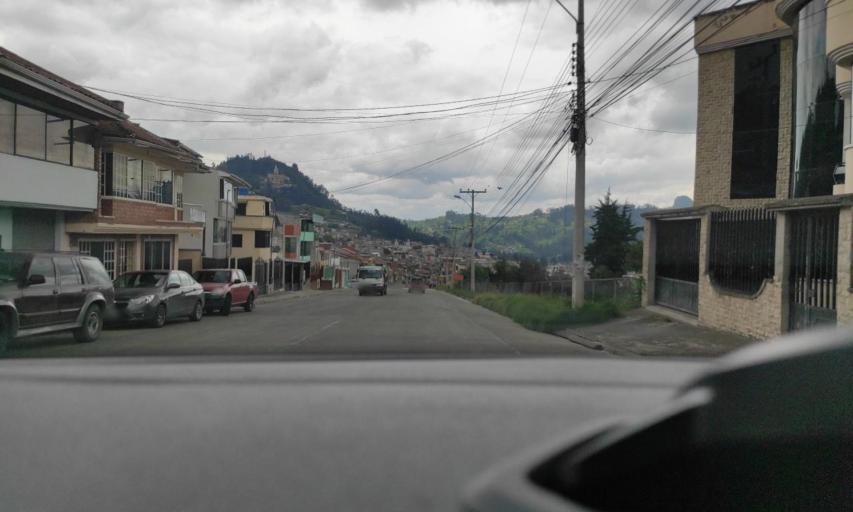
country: EC
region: Canar
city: Azogues
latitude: -2.7062
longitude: -78.8922
